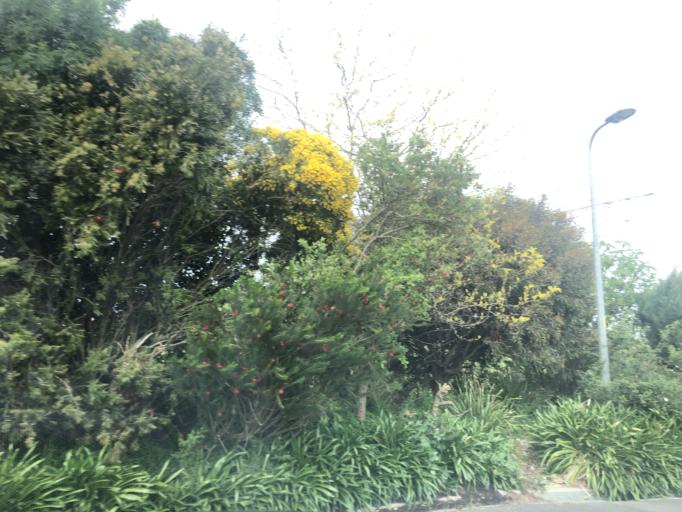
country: AU
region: Victoria
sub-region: Casey
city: Hallam
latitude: -38.0152
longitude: 145.2836
